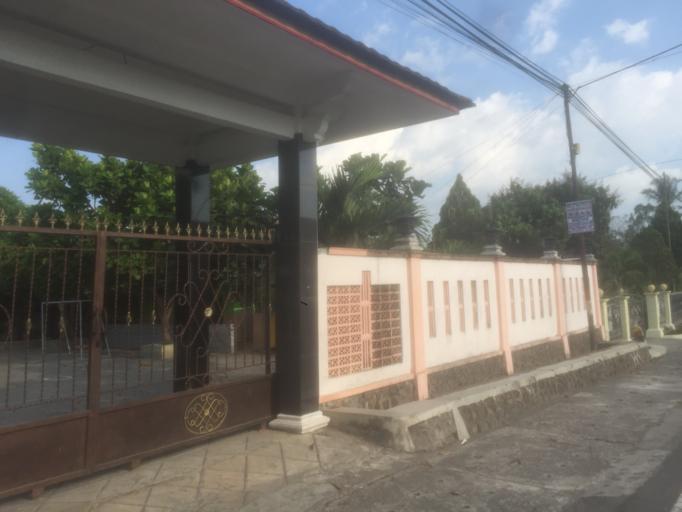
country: ID
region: Daerah Istimewa Yogyakarta
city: Sleman
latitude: -7.6393
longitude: 110.4256
